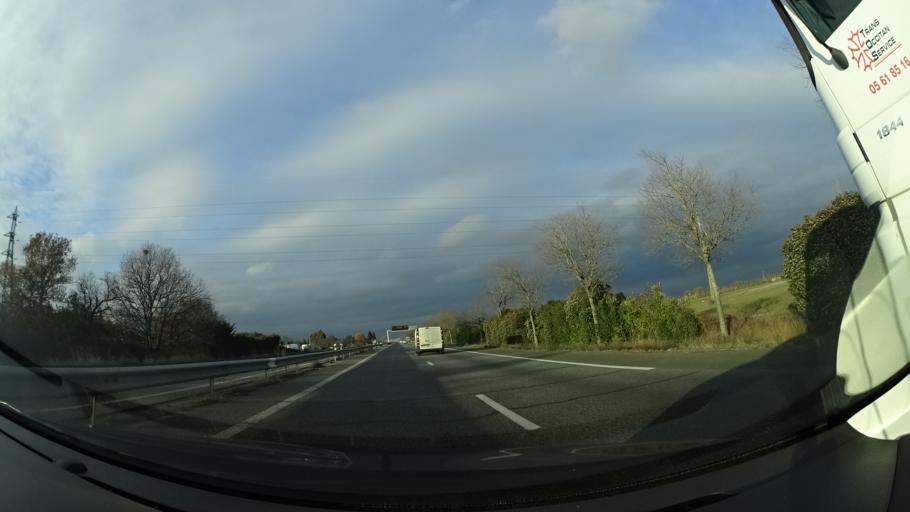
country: FR
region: Midi-Pyrenees
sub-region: Departement de l'Ariege
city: La Tour-du-Crieu
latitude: 43.1191
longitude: 1.6299
